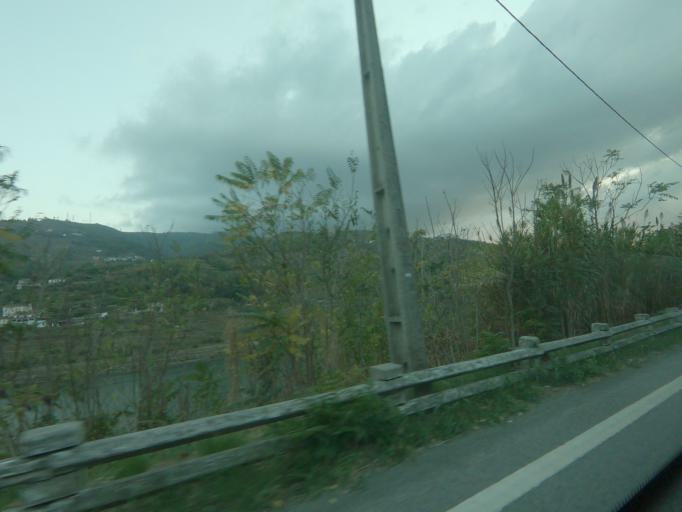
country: PT
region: Vila Real
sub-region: Peso da Regua
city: Godim
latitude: 41.1531
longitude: -7.8276
